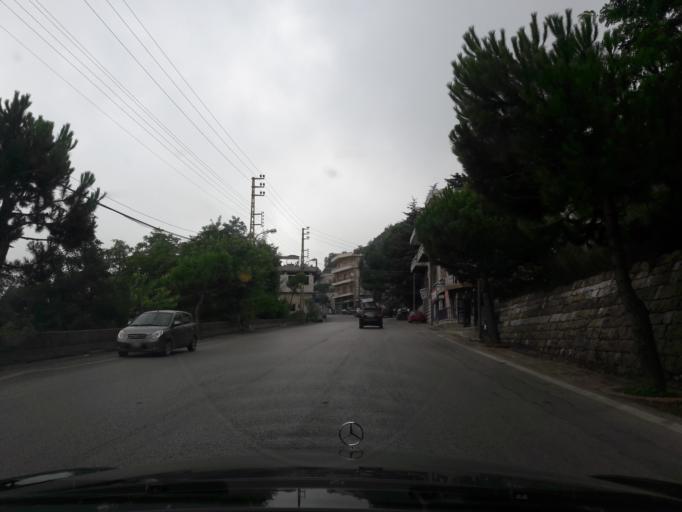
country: LB
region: Mont-Liban
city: Djounie
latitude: 33.9183
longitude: 35.6702
